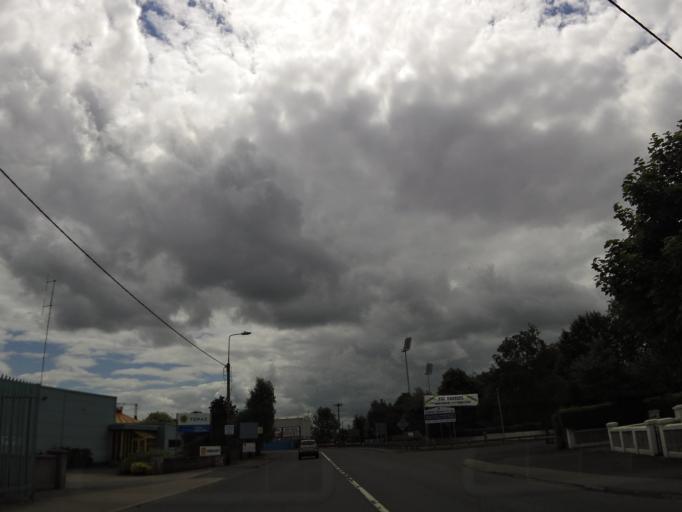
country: IE
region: Munster
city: Thurles
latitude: 52.6847
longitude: -7.8246
